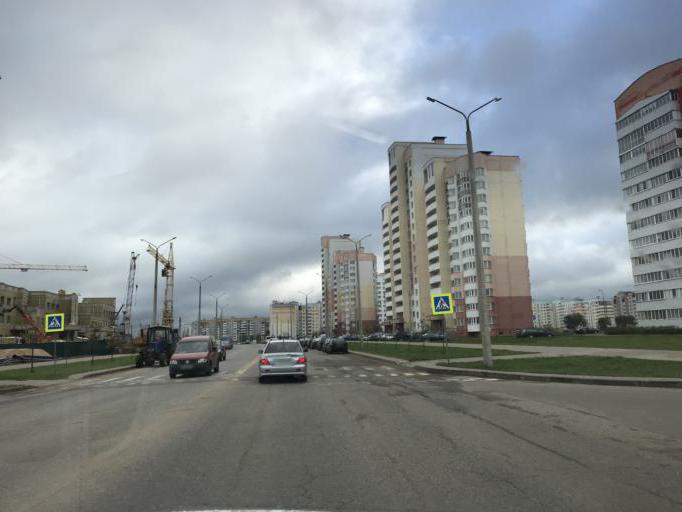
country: BY
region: Mogilev
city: Mahilyow
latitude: 53.8825
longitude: 30.3588
